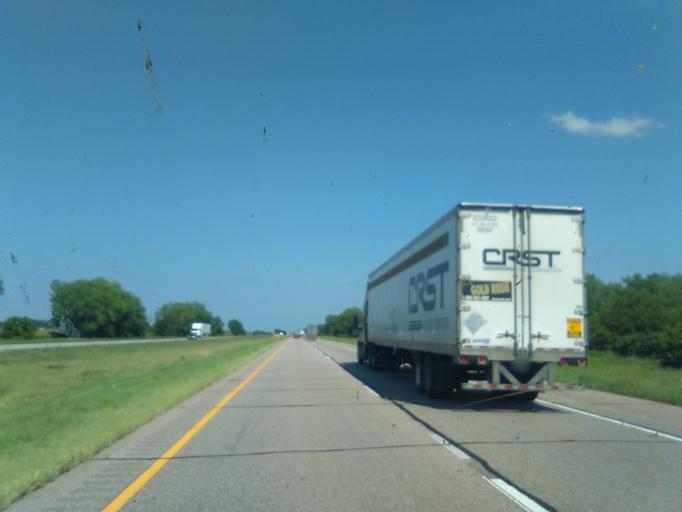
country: US
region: Nebraska
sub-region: Buffalo County
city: Kearney
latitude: 40.6725
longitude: -99.1979
